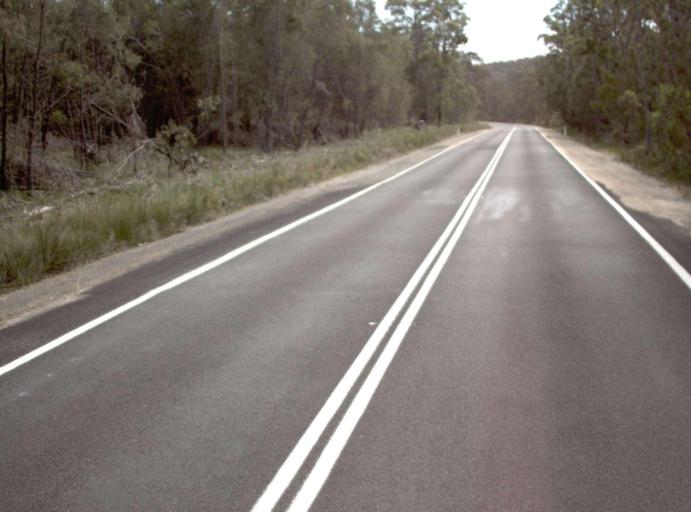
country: AU
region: New South Wales
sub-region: Bega Valley
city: Eden
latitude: -37.4483
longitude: 149.6245
